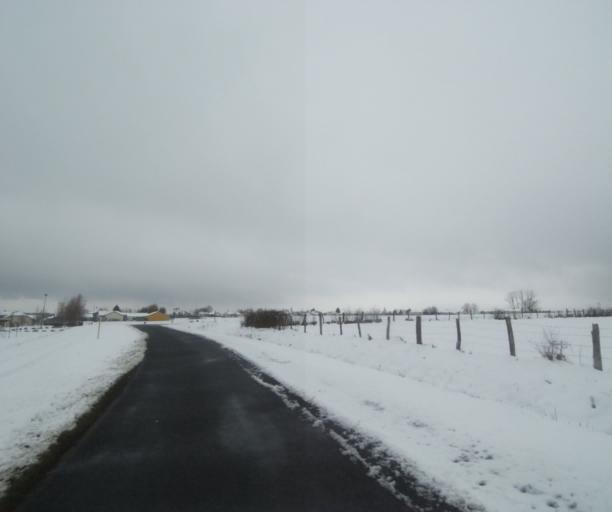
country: FR
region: Champagne-Ardenne
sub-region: Departement de la Haute-Marne
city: Laneuville-a-Remy
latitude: 48.5083
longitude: 4.8721
